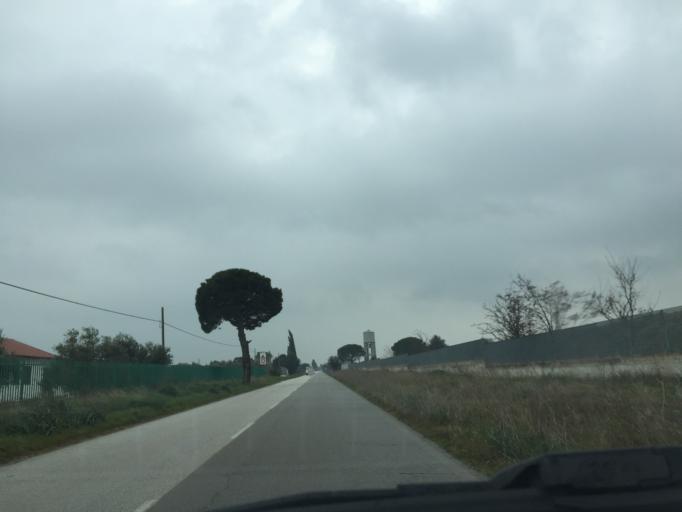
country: IT
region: Apulia
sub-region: Provincia di Foggia
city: Foggia
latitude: 41.4277
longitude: 15.4704
